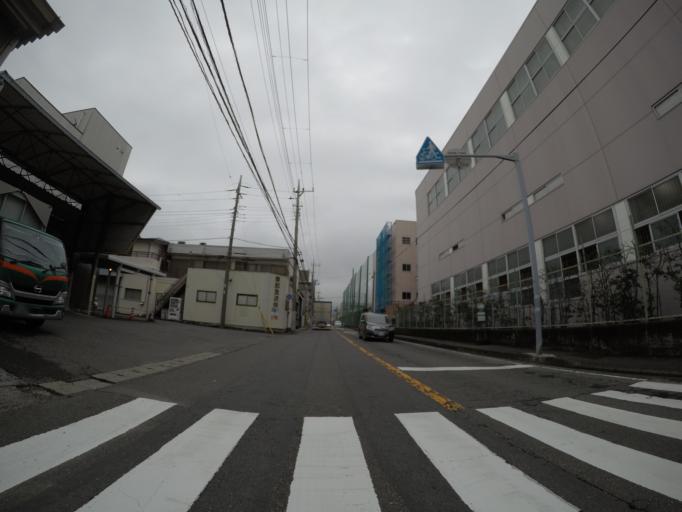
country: JP
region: Shizuoka
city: Numazu
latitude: 35.1131
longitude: 138.8523
